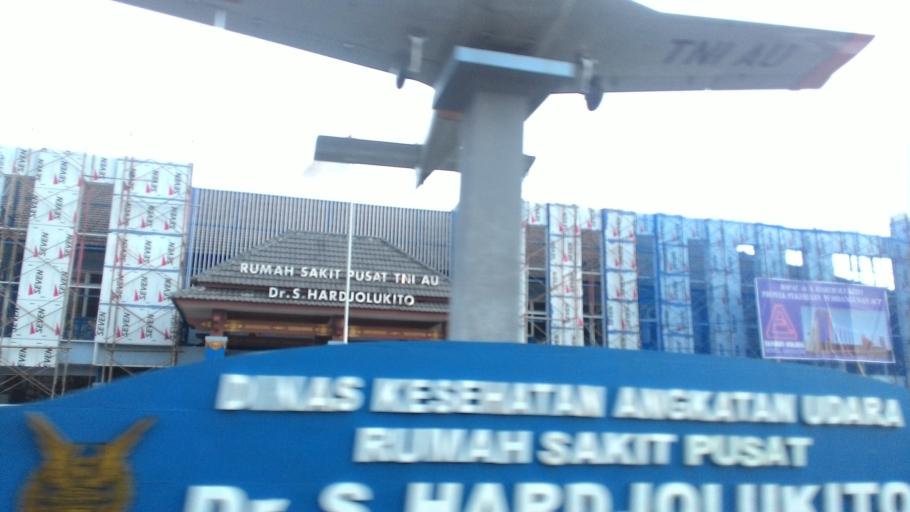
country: ID
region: Daerah Istimewa Yogyakarta
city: Depok
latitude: -7.7976
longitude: 110.4101
